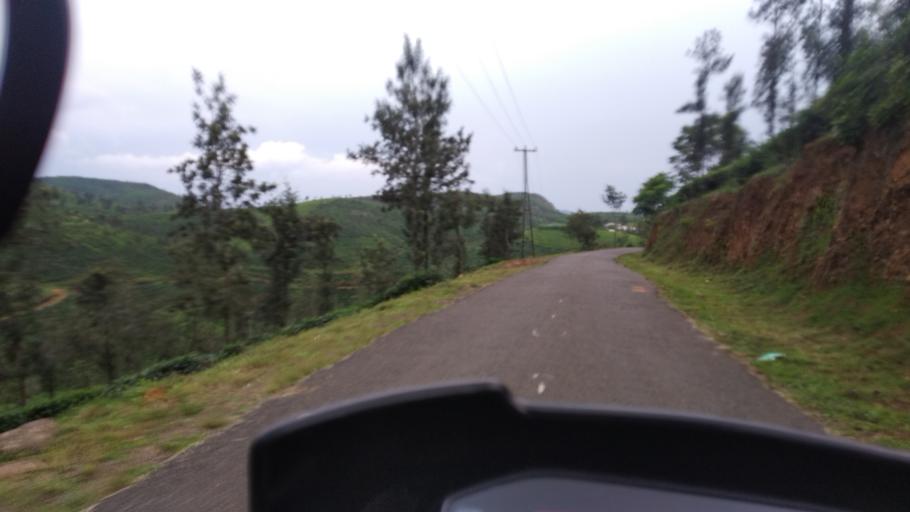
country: IN
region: Tamil Nadu
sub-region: Theni
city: Gudalur
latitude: 9.5407
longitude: 77.0433
